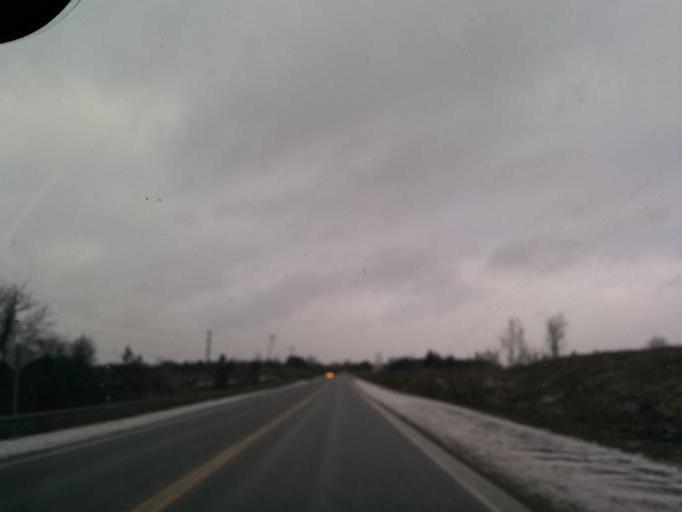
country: CA
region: Ontario
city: Orangeville
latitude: 43.8503
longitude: -80.0076
